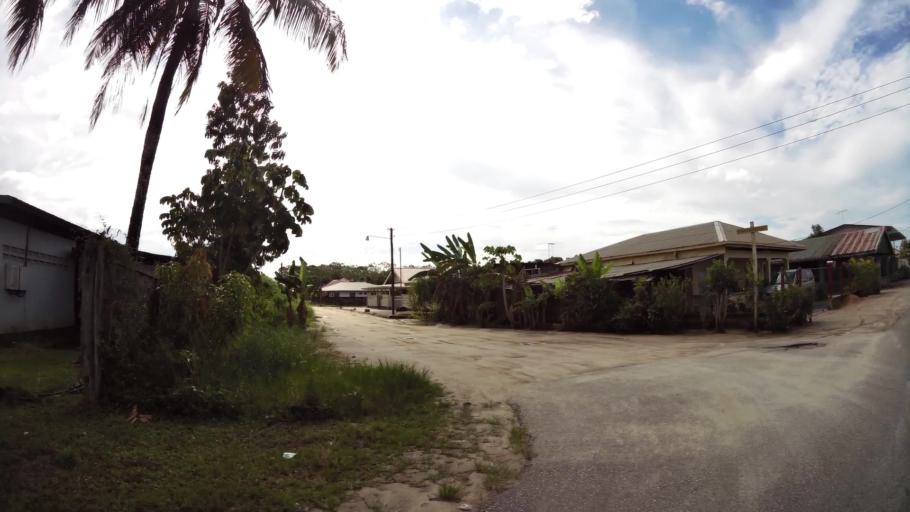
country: SR
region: Paramaribo
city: Paramaribo
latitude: 5.8488
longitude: -55.2082
